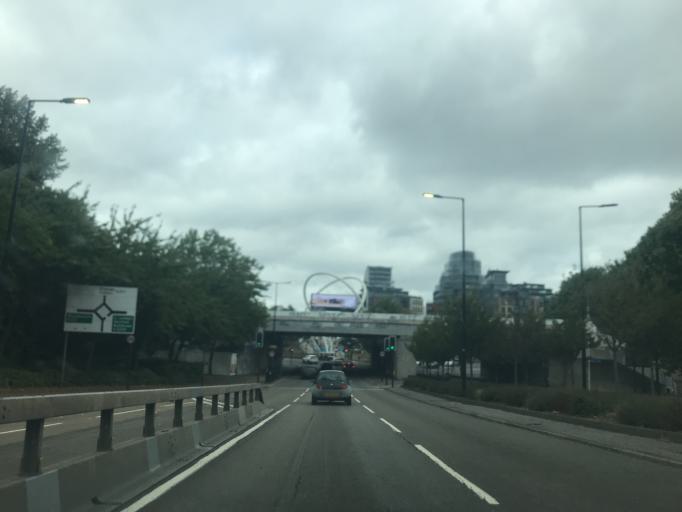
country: GB
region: England
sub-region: Greater London
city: Earlsfield
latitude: 51.4607
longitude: -0.1841
